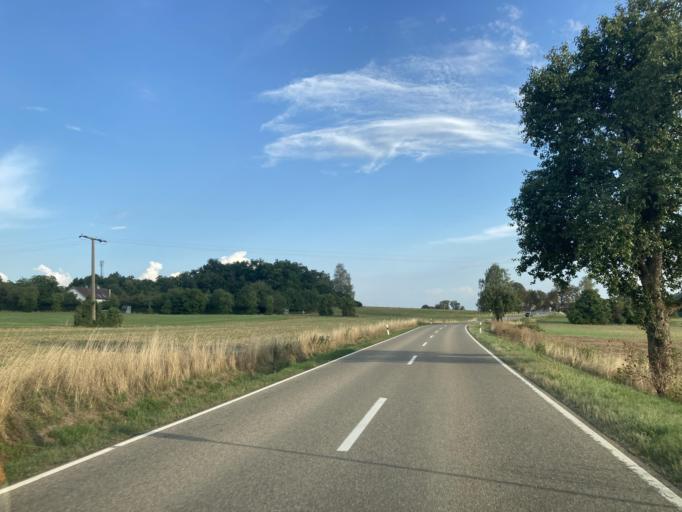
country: DE
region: Baden-Wuerttemberg
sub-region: Regierungsbezirk Stuttgart
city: Dischingen
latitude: 48.6886
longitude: 10.3648
